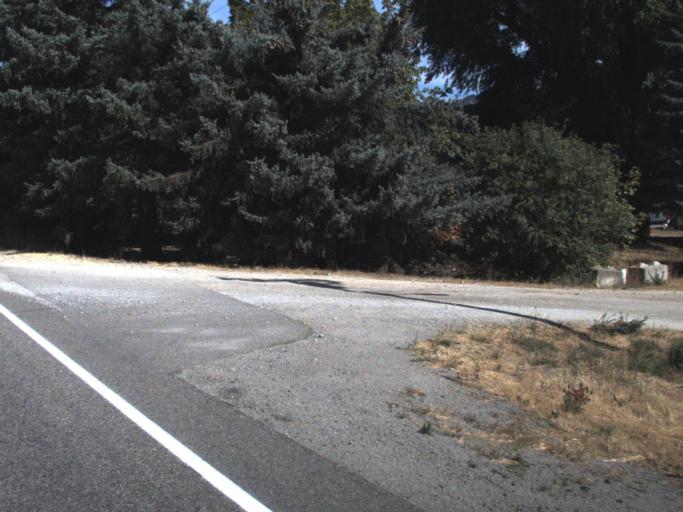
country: US
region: Washington
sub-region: Stevens County
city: Chewelah
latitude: 48.2660
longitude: -117.7153
